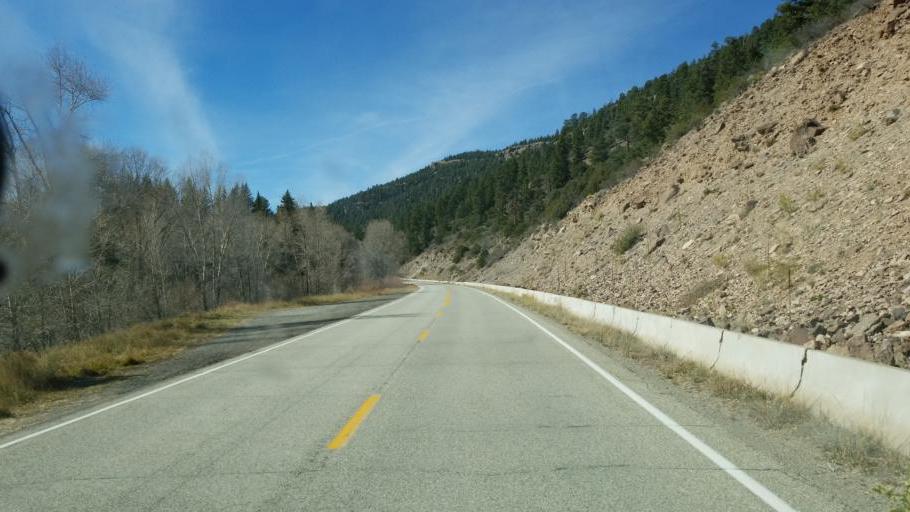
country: US
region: Colorado
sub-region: Conejos County
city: Conejos
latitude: 37.0711
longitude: -106.2557
